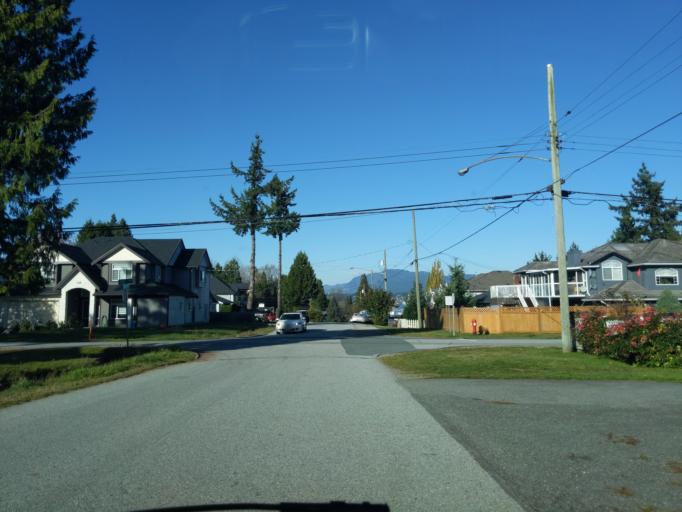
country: CA
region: British Columbia
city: New Westminster
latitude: 49.2025
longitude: -122.8578
